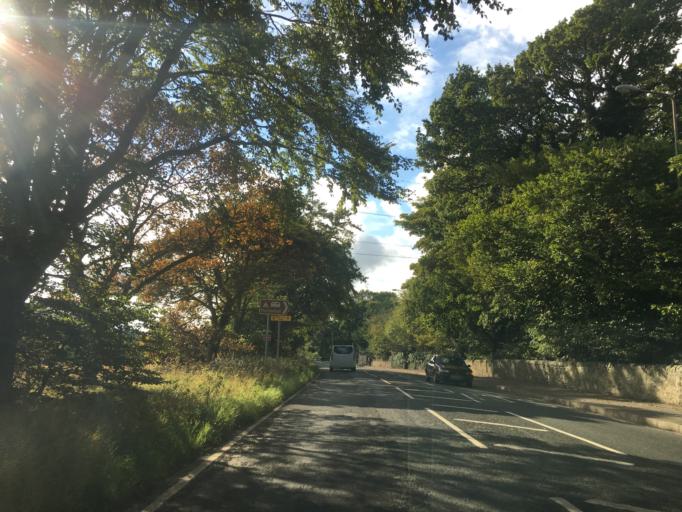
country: GB
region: Scotland
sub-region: Midlothian
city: Loanhead
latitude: 55.8997
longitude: -3.1733
